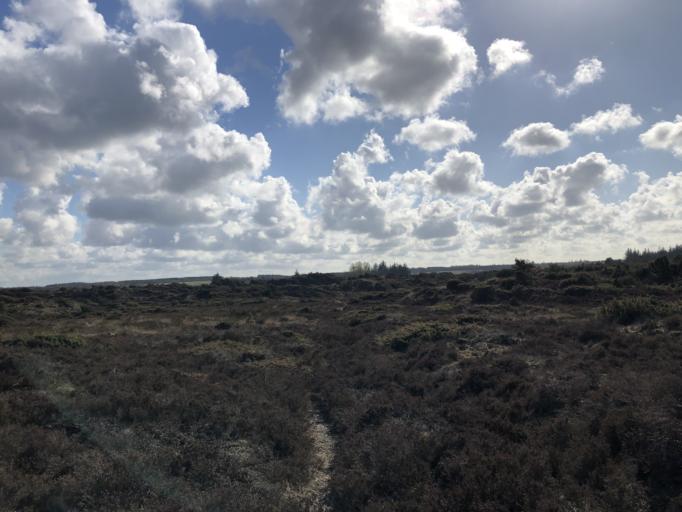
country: DK
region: Central Jutland
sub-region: Holstebro Kommune
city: Ulfborg
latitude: 56.2565
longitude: 8.4145
